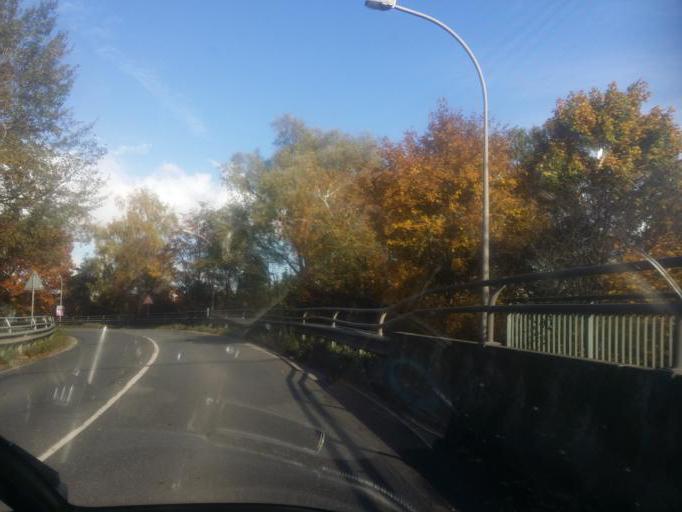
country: DE
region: Schleswig-Holstein
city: Kummerfeld
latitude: 53.6826
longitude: 9.7934
